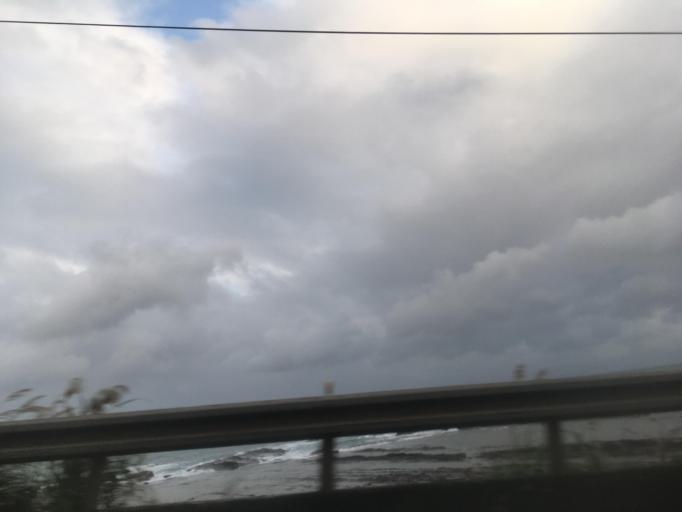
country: TW
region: Taiwan
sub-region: Keelung
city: Keelung
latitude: 24.9599
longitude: 121.9189
